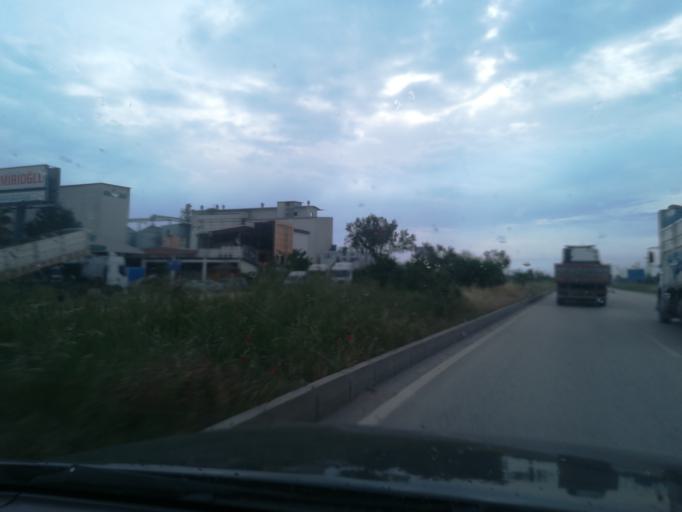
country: TR
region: Adana
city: Yuregir
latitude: 36.9809
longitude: 35.4437
